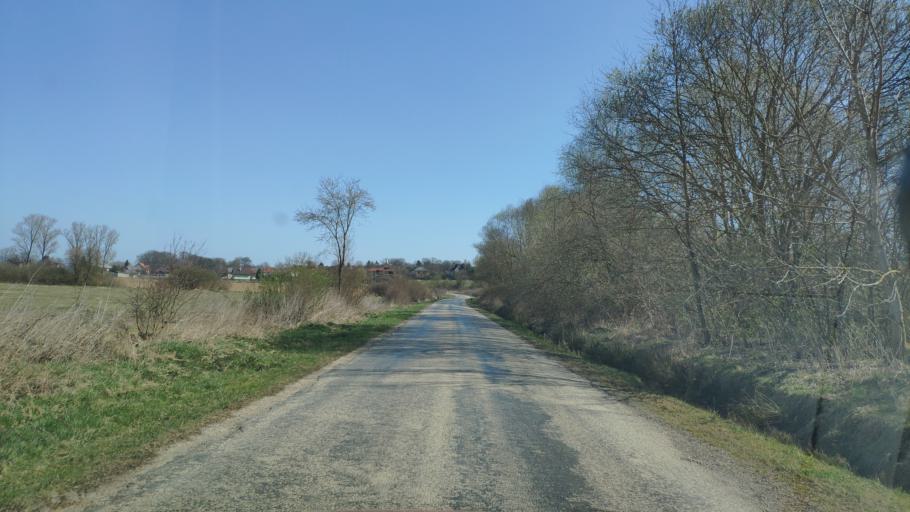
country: SK
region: Kosicky
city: Moldava nad Bodvou
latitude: 48.5616
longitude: 20.9527
